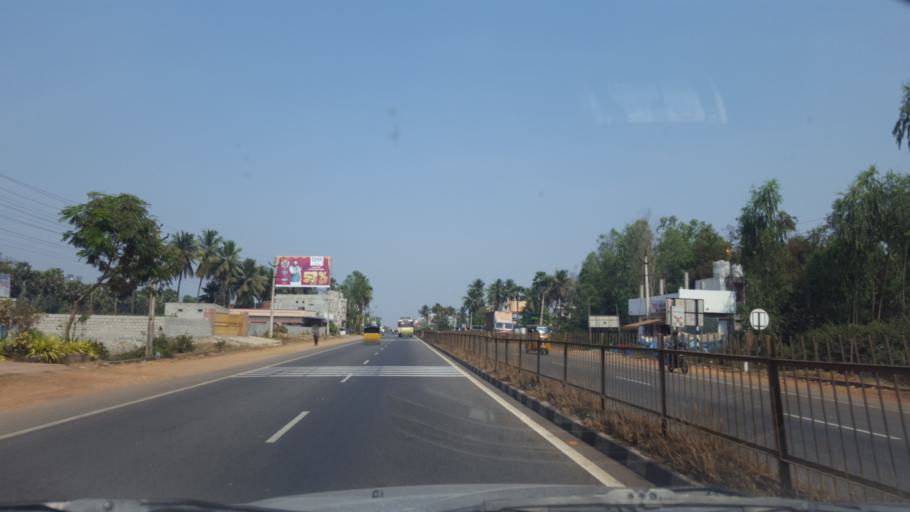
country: IN
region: Andhra Pradesh
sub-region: Vishakhapatnam
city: Anakapalle
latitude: 17.6772
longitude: 82.9762
